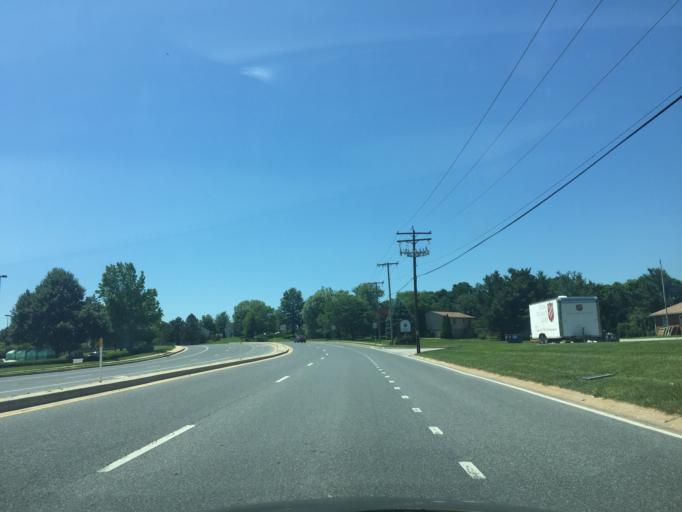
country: US
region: Maryland
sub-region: Carroll County
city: Westminster
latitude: 39.5867
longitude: -76.9840
